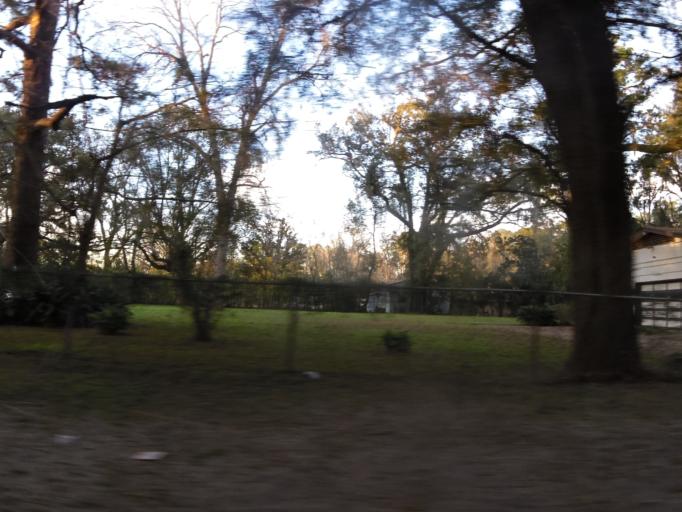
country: US
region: Florida
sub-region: Duval County
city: Jacksonville
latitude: 30.2796
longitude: -81.6424
